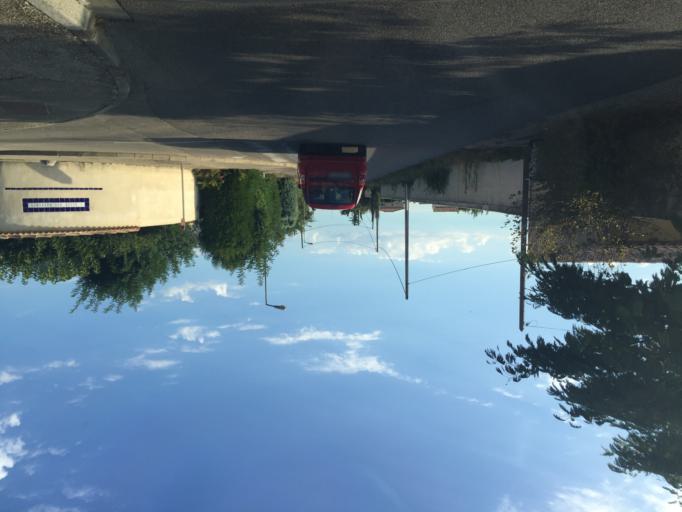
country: FR
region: Provence-Alpes-Cote d'Azur
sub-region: Departement du Vaucluse
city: Pernes-les-Fontaines
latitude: 44.0068
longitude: 5.0558
